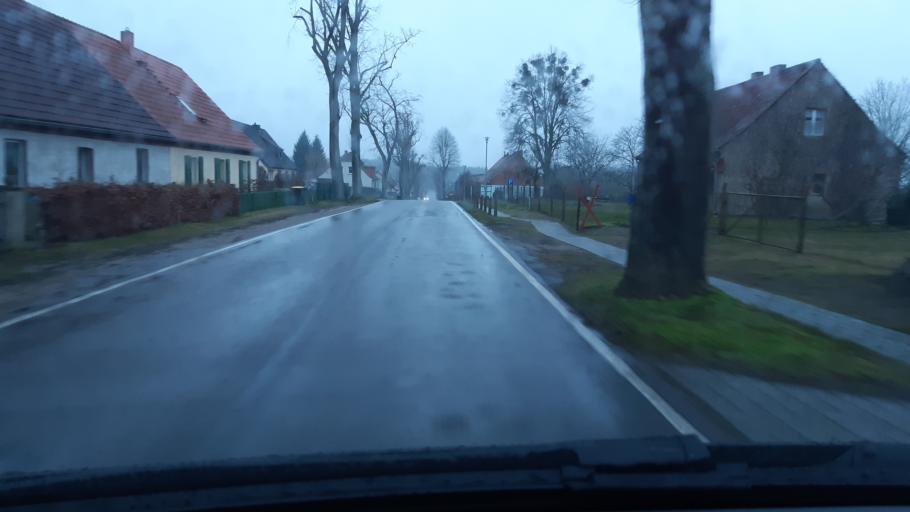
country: DE
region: Brandenburg
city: Mittenwalde
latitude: 53.1622
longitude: 13.6288
